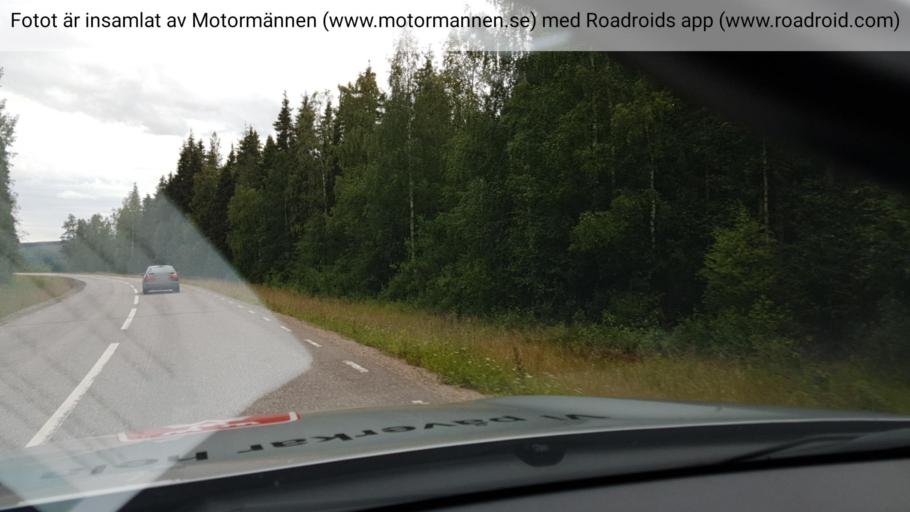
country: SE
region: Norrbotten
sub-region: Overkalix Kommun
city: OEverkalix
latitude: 66.6239
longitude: 22.7696
